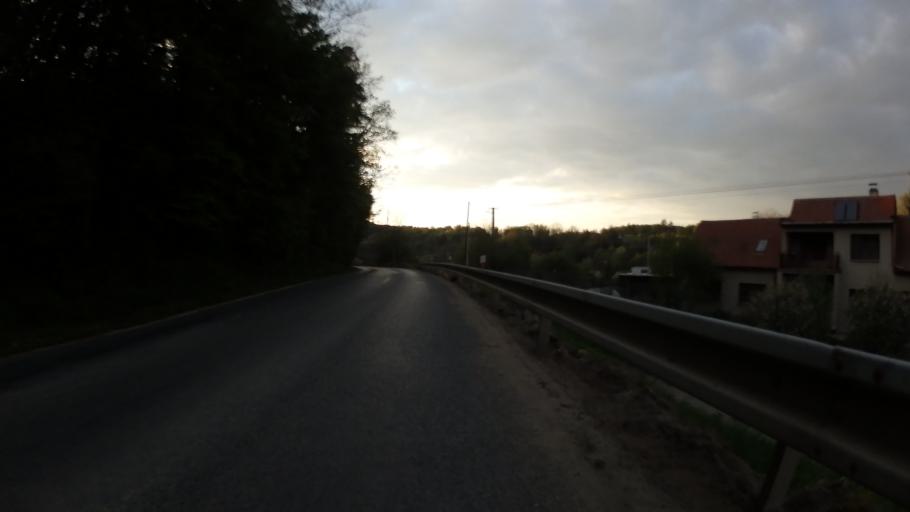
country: CZ
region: South Moravian
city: Strelice
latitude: 49.1361
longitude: 16.4745
